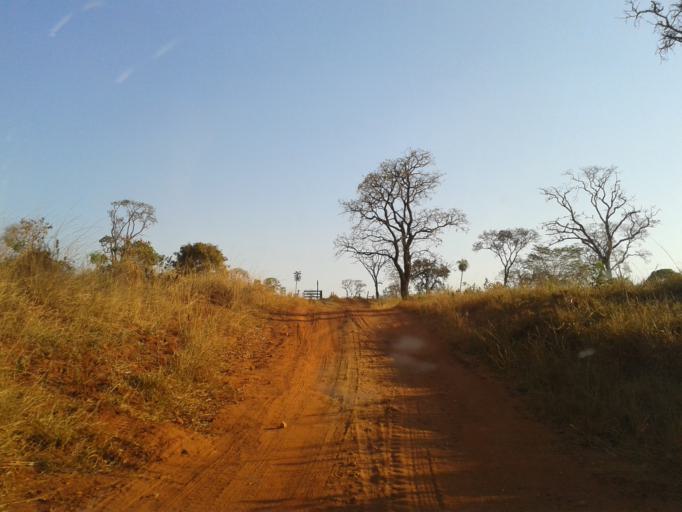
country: BR
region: Minas Gerais
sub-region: Ituiutaba
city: Ituiutaba
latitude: -19.2440
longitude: -49.6081
